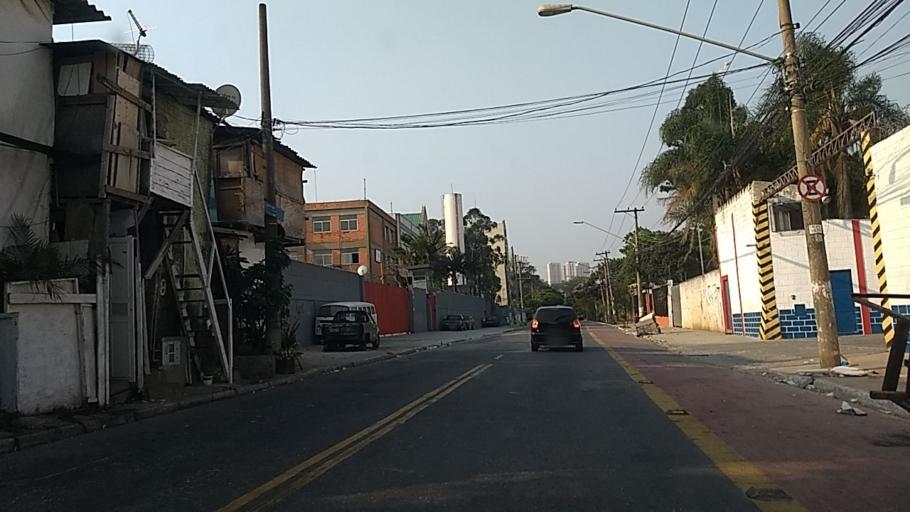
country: BR
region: Sao Paulo
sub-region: Sao Paulo
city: Sao Paulo
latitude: -23.5126
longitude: -46.6024
